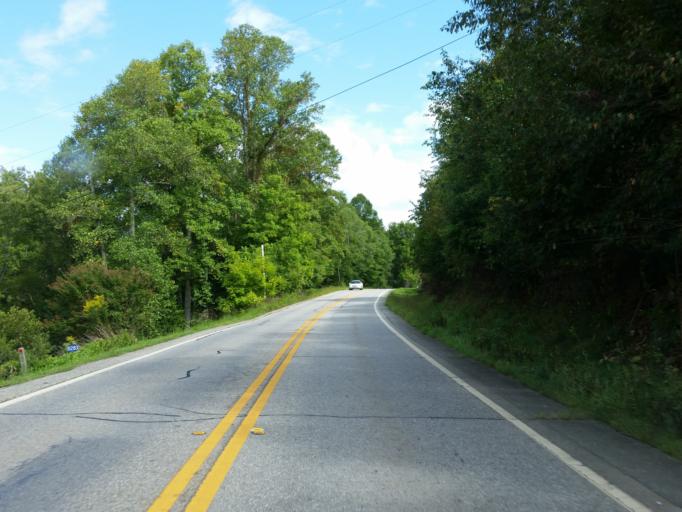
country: US
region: Georgia
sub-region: Fannin County
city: Blue Ridge
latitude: 34.8846
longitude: -84.2564
